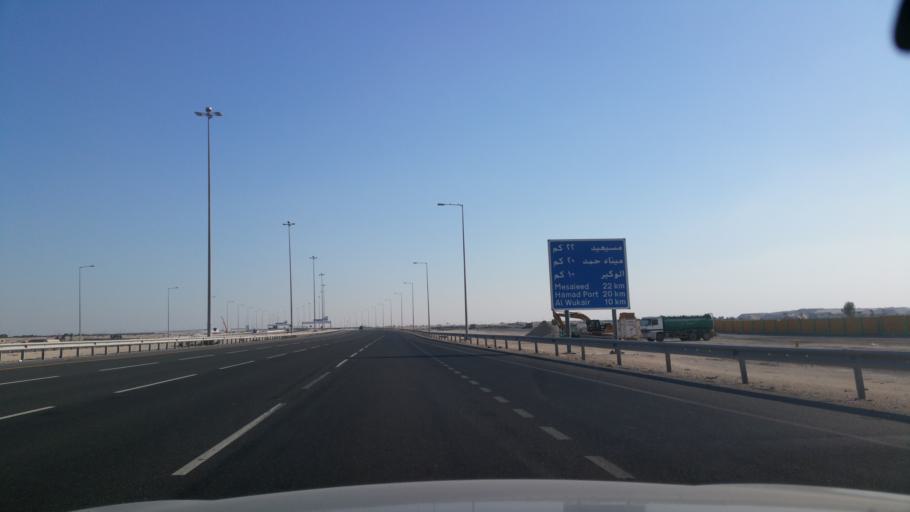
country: QA
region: Al Wakrah
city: Al Wukayr
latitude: 25.1485
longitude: 51.4745
